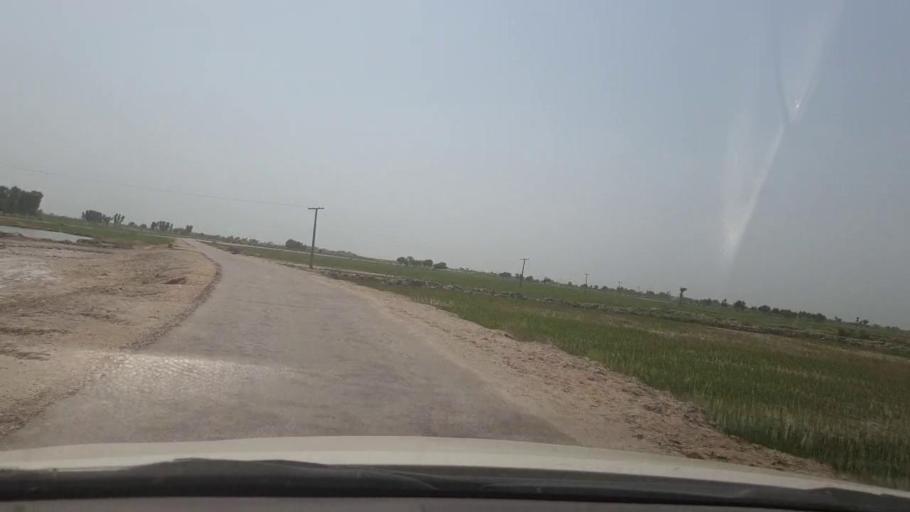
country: PK
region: Sindh
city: Shikarpur
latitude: 27.9936
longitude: 68.5614
